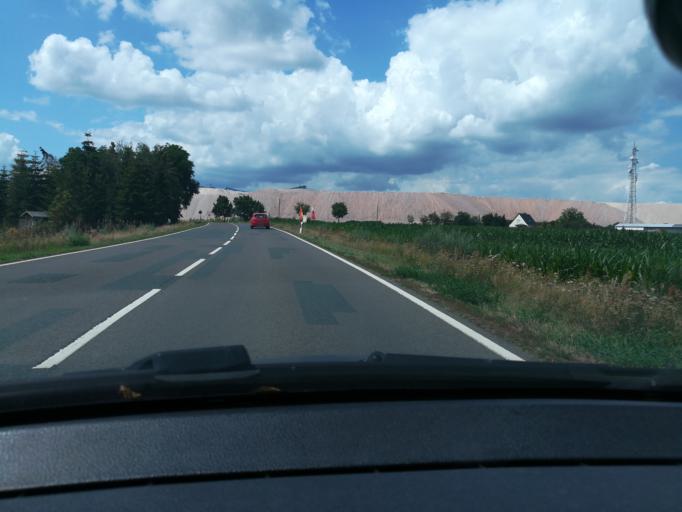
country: DE
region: Saxony-Anhalt
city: Zielitz
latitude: 52.3013
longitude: 11.7059
